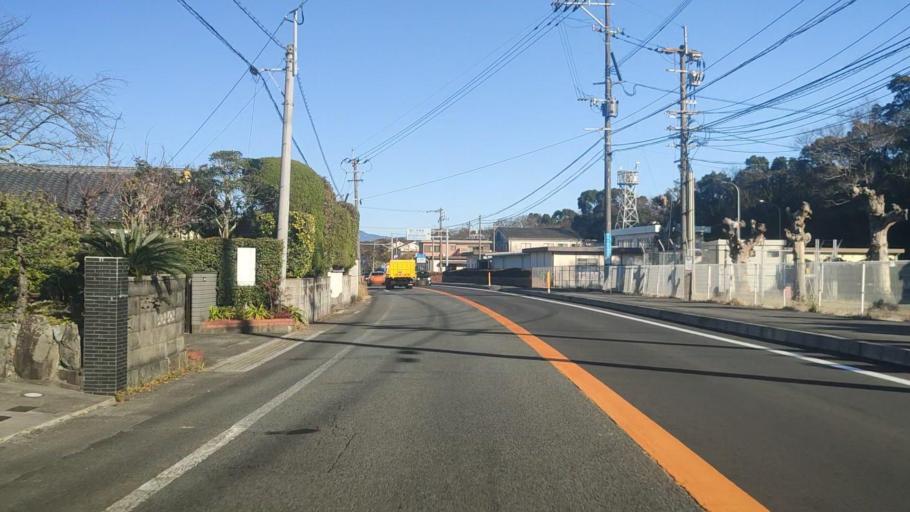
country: JP
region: Miyazaki
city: Nobeoka
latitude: 32.5215
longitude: 131.6836
